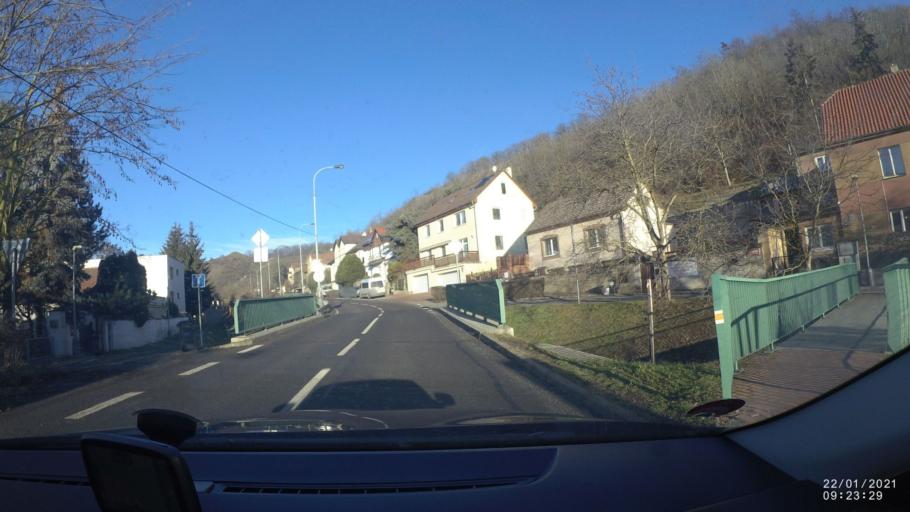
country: CZ
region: Praha
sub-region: Praha 12
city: Modrany
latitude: 50.0128
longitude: 14.3799
